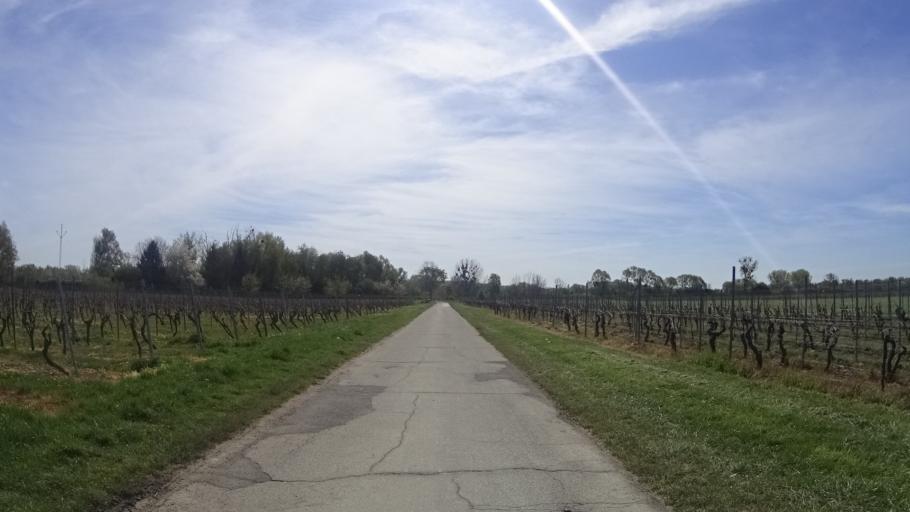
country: DE
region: Rheinland-Pfalz
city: Dienheim
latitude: 49.8331
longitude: 8.3637
